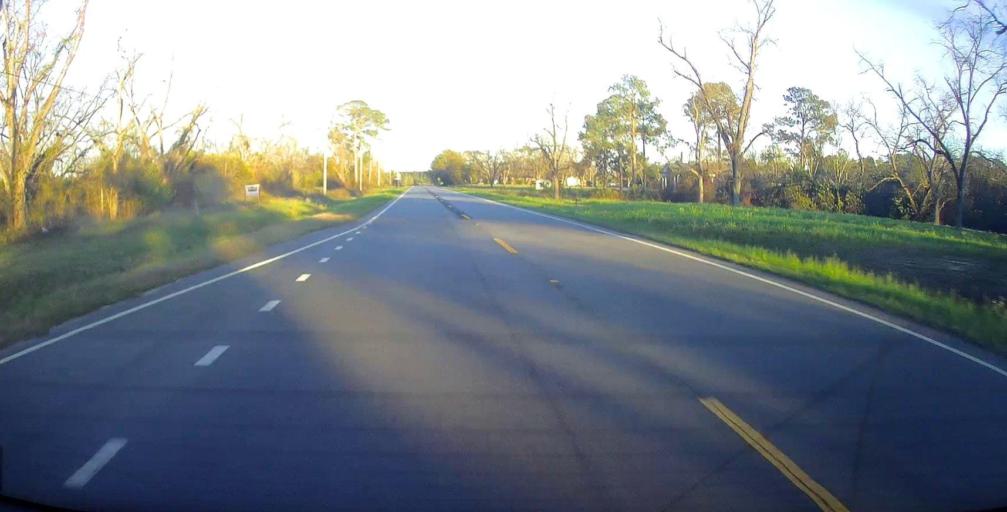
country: US
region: Georgia
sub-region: Crisp County
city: Cordele
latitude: 31.9572
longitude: -83.7361
